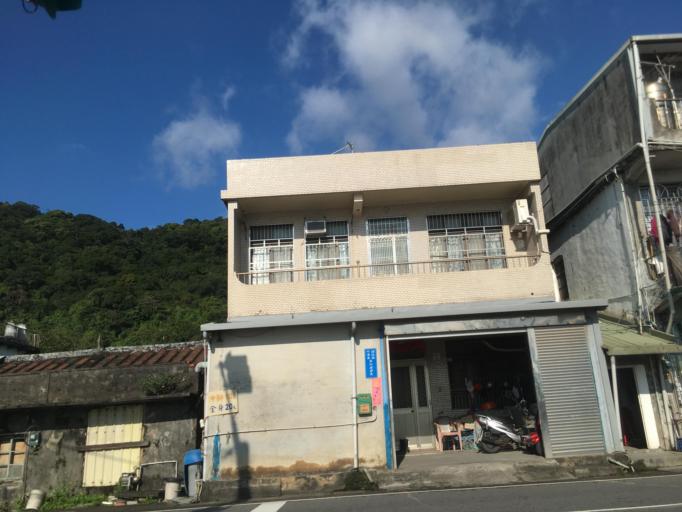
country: TW
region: Taiwan
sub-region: Yilan
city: Yilan
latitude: 24.8878
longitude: 121.8487
